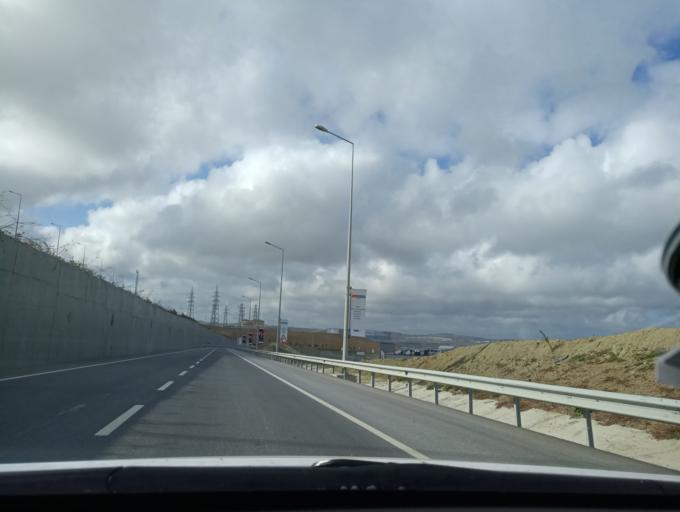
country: TR
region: Istanbul
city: Durusu
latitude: 41.2457
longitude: 28.7512
